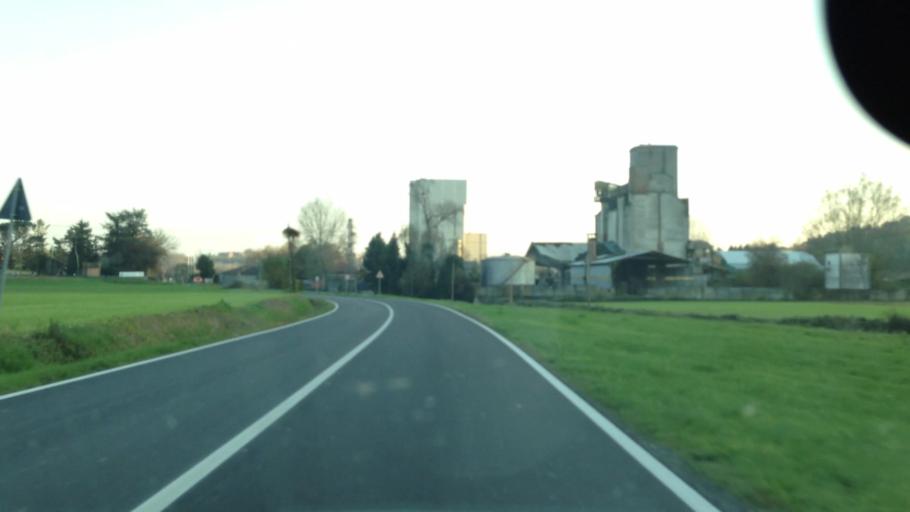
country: IT
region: Piedmont
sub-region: Provincia di Asti
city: Montiglio
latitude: 45.0726
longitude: 8.1037
